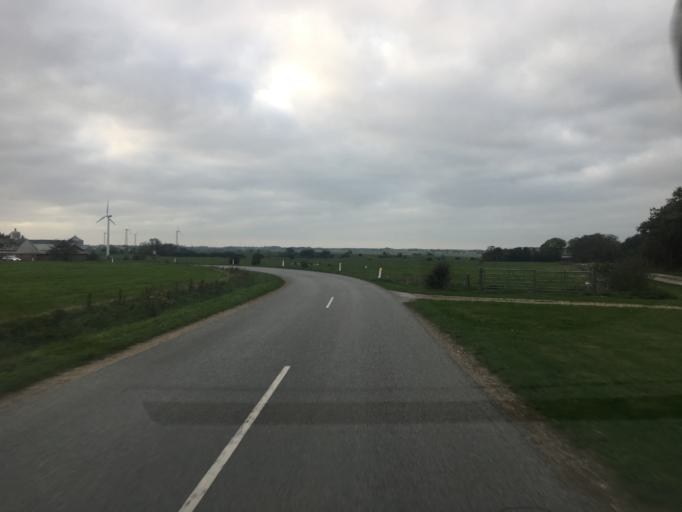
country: DE
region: Schleswig-Holstein
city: Aventoft
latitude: 54.9888
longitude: 8.7614
